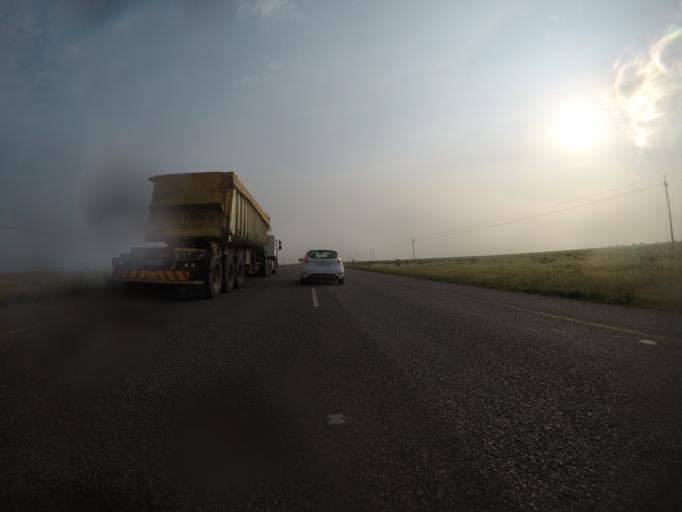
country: ZA
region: Western Cape
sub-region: West Coast District Municipality
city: Malmesbury
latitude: -33.6533
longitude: 18.7093
